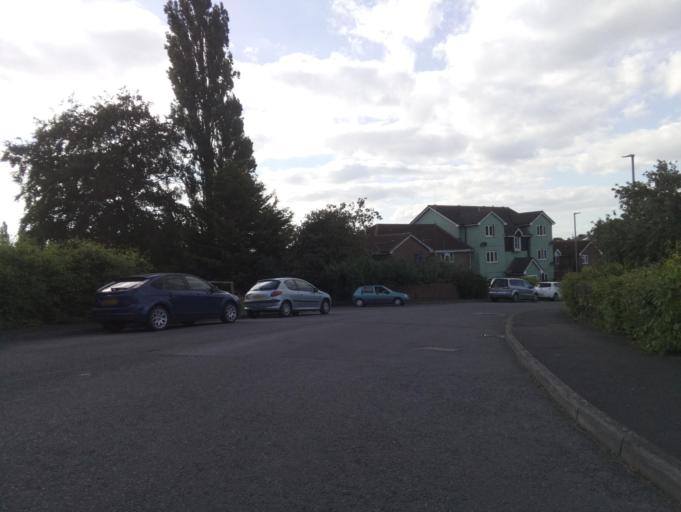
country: GB
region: England
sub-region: Somerset
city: Glastonbury
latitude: 51.1443
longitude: -2.7207
